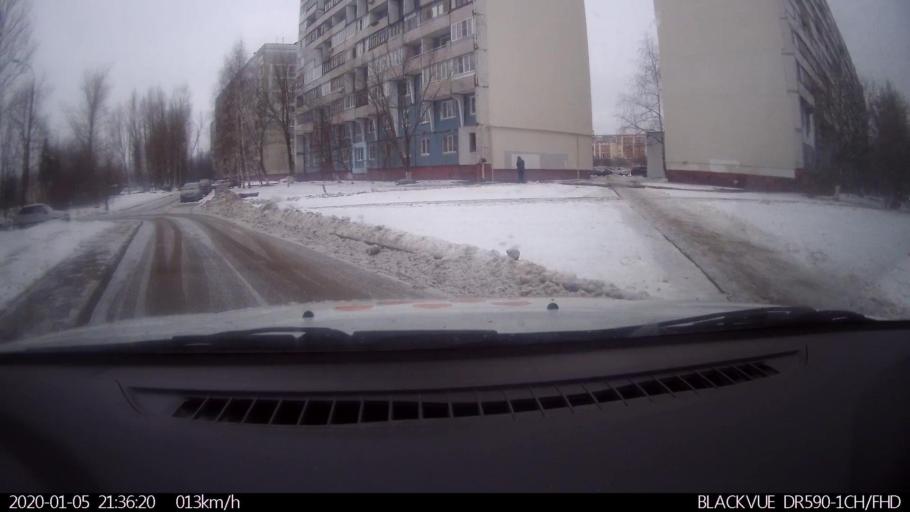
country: RU
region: Nizjnij Novgorod
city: Gorbatovka
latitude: 56.2563
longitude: 43.8444
